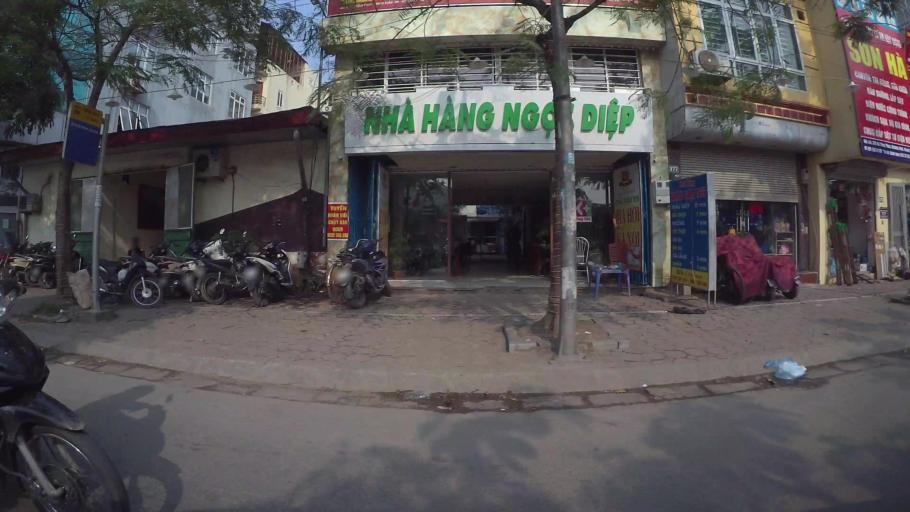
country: VN
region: Ha Noi
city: Thanh Xuan
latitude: 20.9899
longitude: 105.8137
